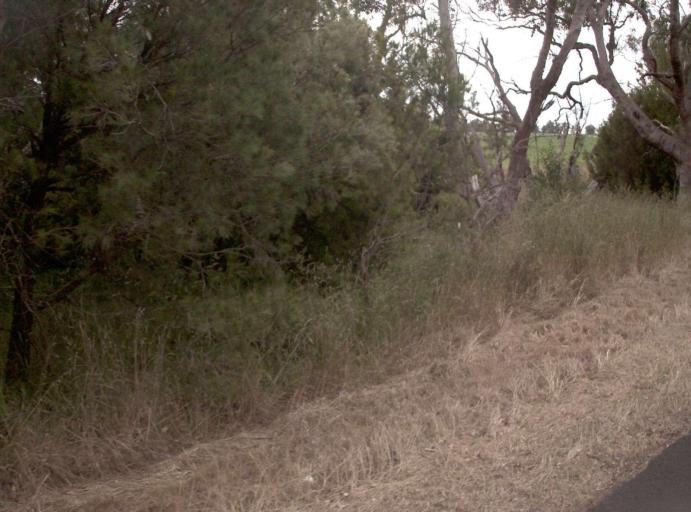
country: AU
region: Victoria
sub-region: Wellington
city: Sale
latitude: -38.3810
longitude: 146.9806
